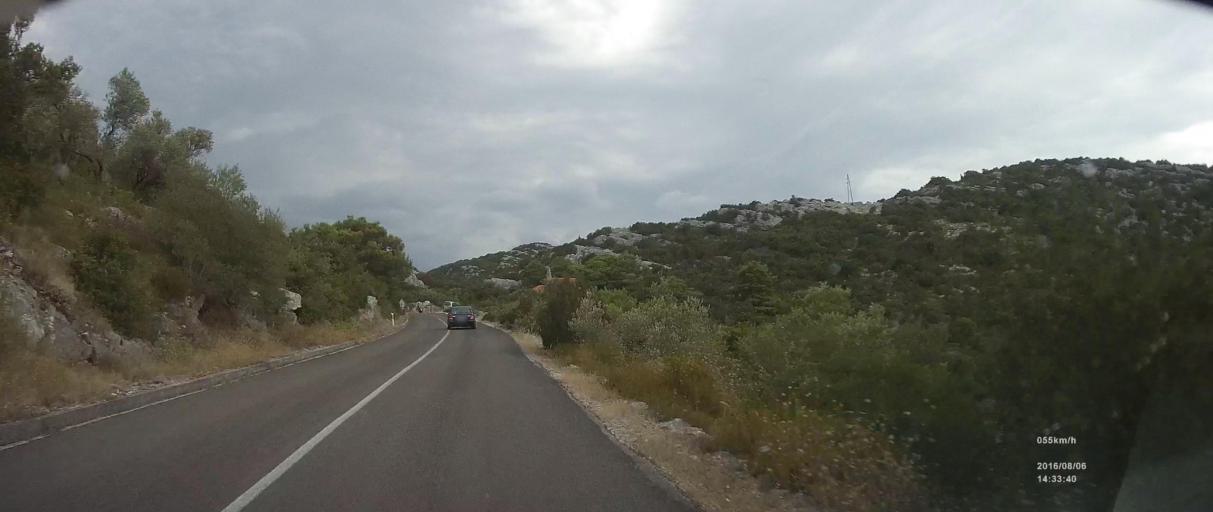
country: HR
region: Dubrovacko-Neretvanska
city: Ston
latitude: 42.7110
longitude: 17.7043
